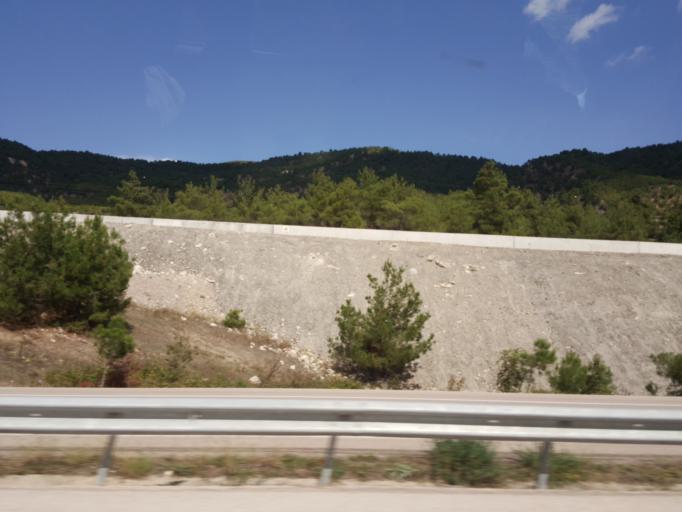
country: TR
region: Tokat
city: Resadiye
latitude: 40.4044
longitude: 37.2656
